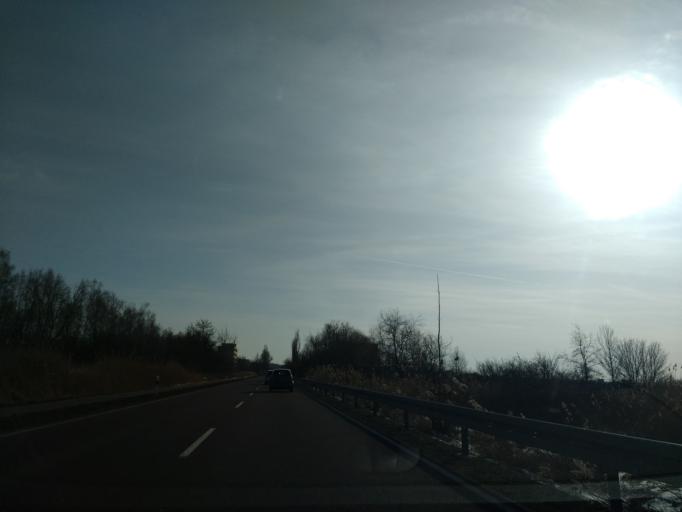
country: DE
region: Saxony-Anhalt
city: Sennewitz
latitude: 51.5317
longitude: 11.9560
